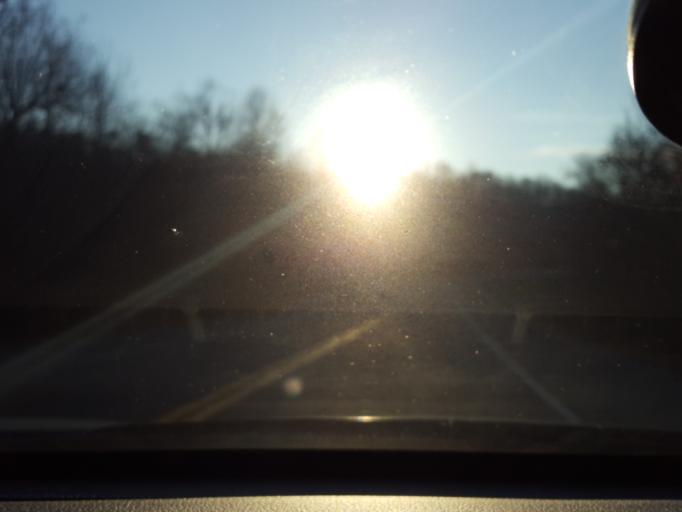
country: US
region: Maryland
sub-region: Calvert County
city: Long Beach
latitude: 38.4496
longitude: -76.4942
